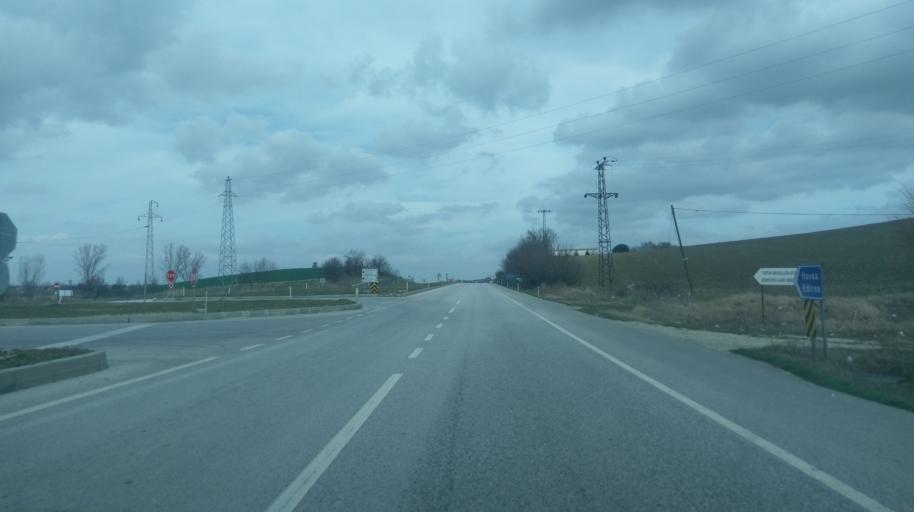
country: TR
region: Edirne
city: Uzun Keupru
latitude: 41.2979
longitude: 26.6959
